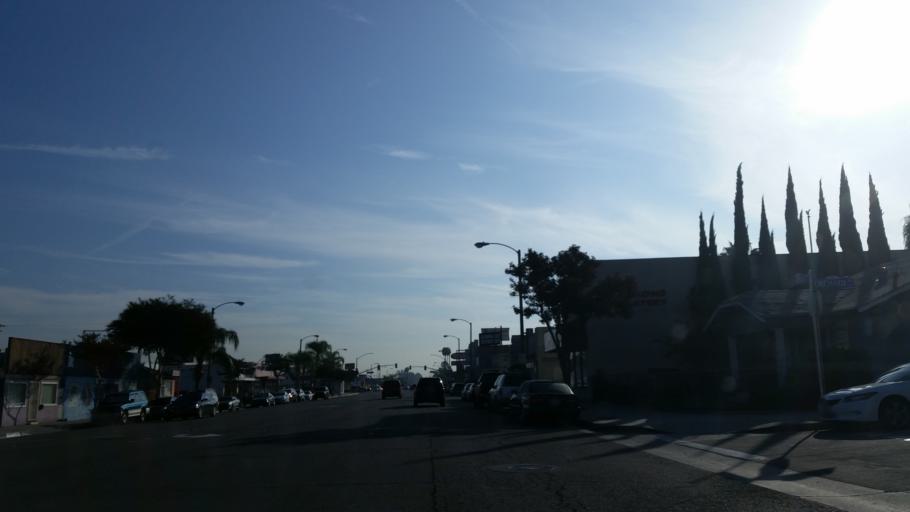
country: US
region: California
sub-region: Los Angeles County
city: Bellflower
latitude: 33.8892
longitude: -118.1279
